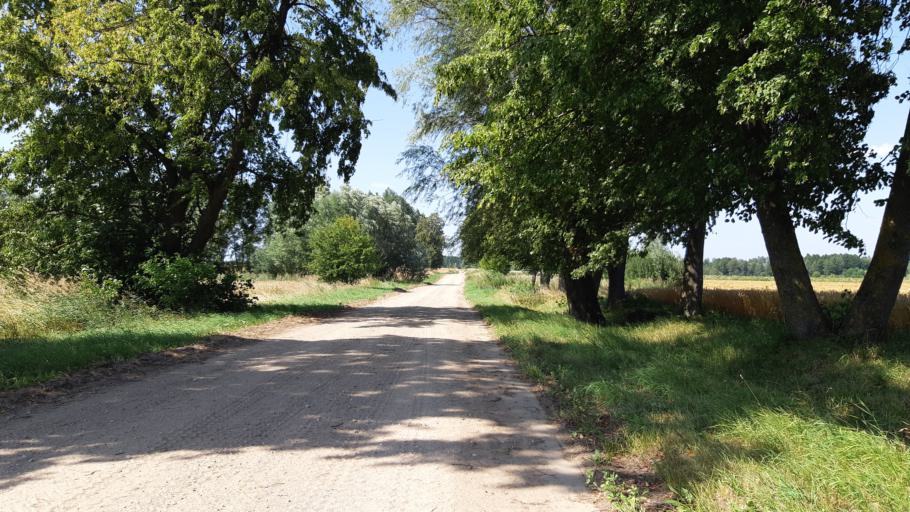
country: LT
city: Virbalis
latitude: 54.6383
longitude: 22.8227
